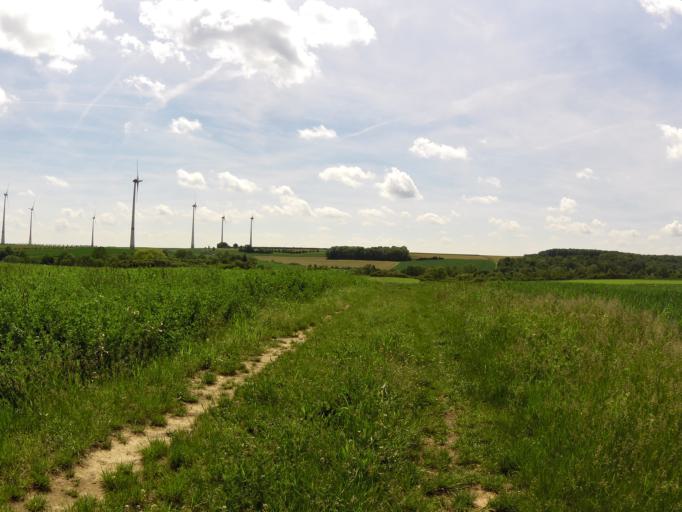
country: DE
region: Bavaria
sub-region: Regierungsbezirk Unterfranken
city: Theilheim
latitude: 49.7267
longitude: 10.0355
